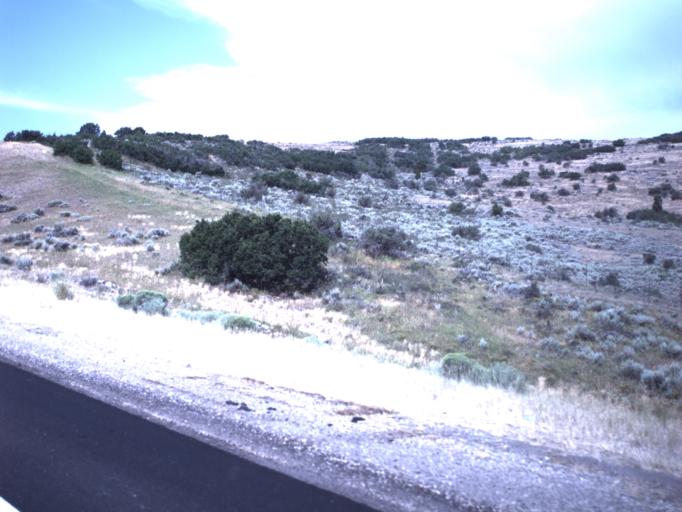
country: US
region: Utah
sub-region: Summit County
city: Kamas
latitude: 40.6368
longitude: -111.3362
